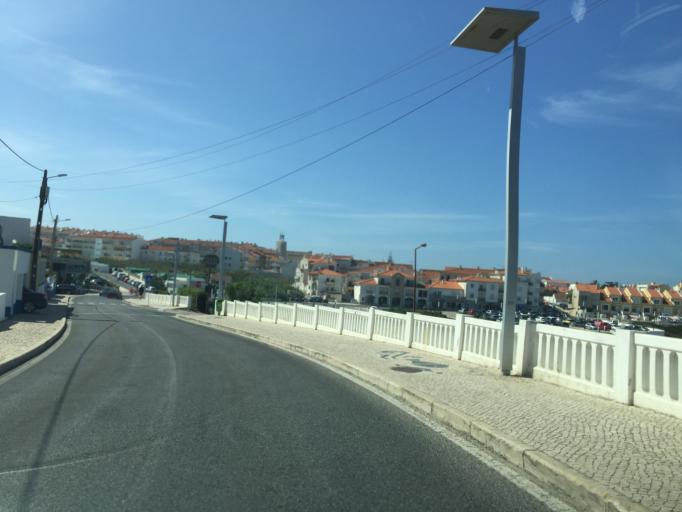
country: PT
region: Lisbon
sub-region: Torres Vedras
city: Silveira
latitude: 39.1377
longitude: -9.3793
